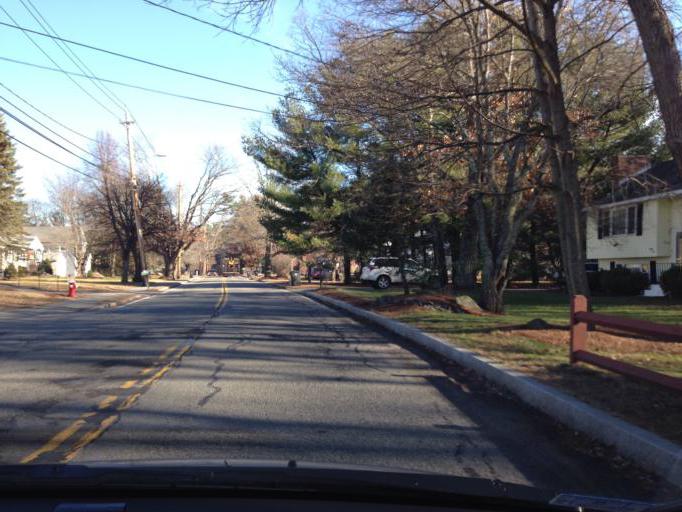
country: US
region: Massachusetts
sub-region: Middlesex County
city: Bedford
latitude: 42.4805
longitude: -71.2821
